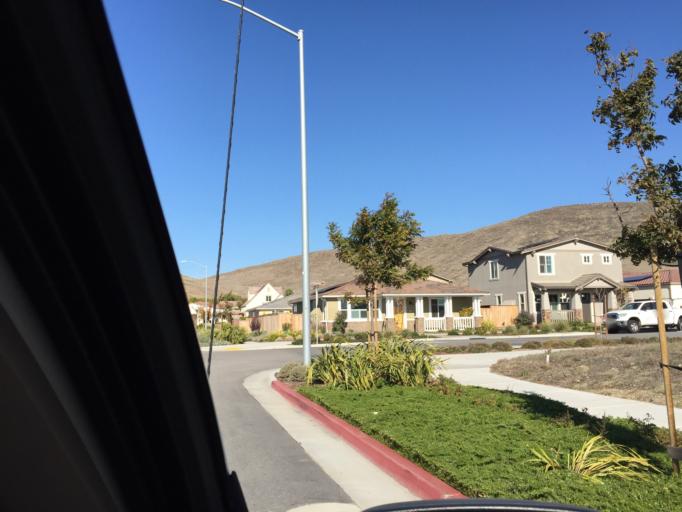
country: US
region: California
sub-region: San Luis Obispo County
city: San Luis Obispo
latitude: 35.2545
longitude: -120.6625
